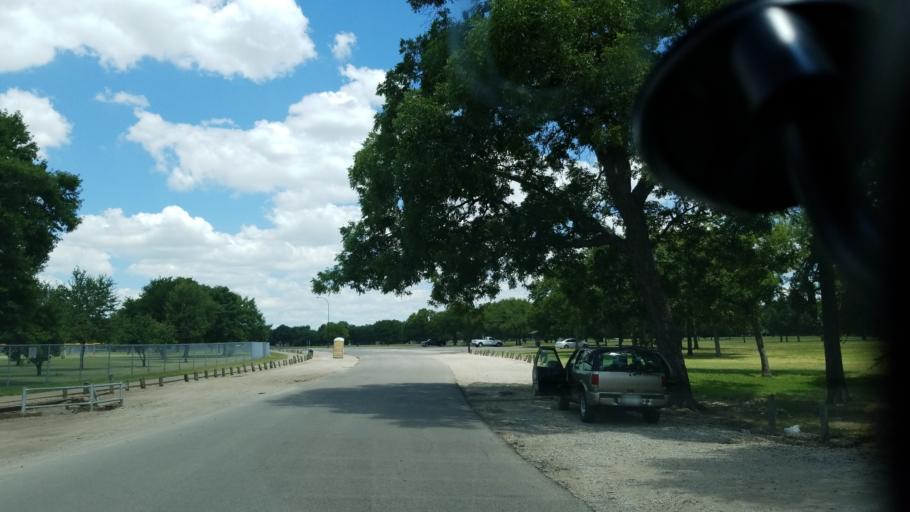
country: US
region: Texas
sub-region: Dallas County
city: Cockrell Hill
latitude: 32.7104
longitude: -96.8505
